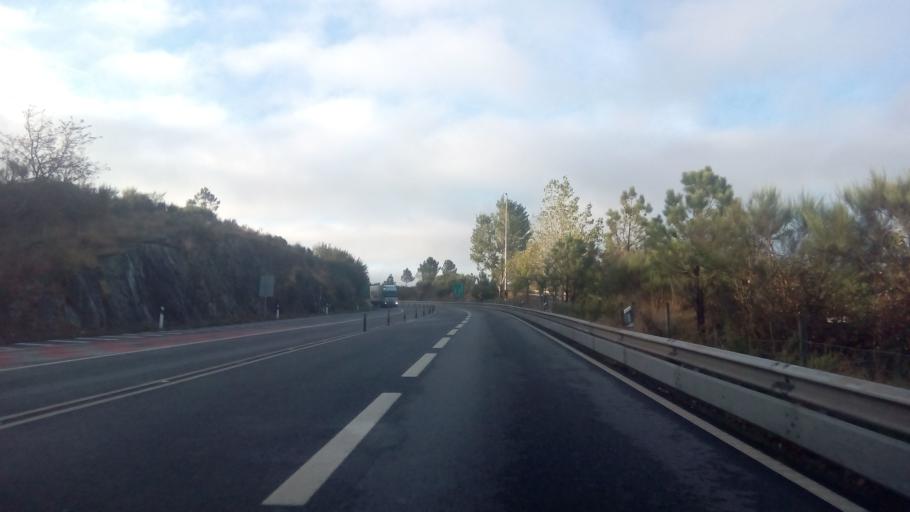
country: PT
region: Porto
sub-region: Amarante
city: Amarante
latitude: 41.2738
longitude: -7.9921
